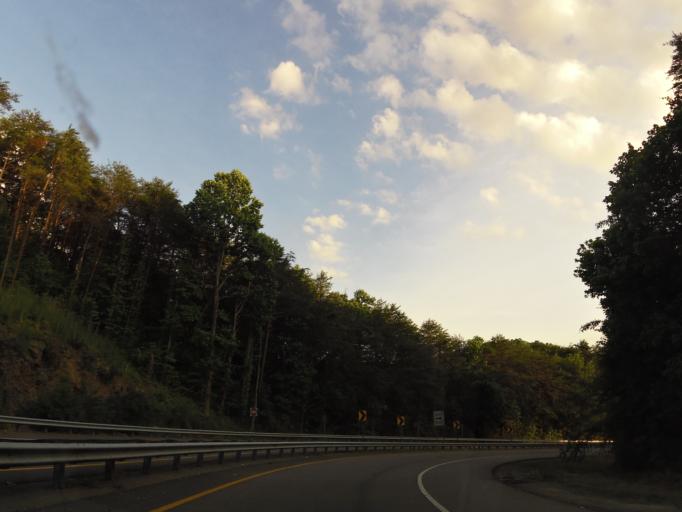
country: US
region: Georgia
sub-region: Walker County
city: Lookout Mountain
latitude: 34.9768
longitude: -85.4158
